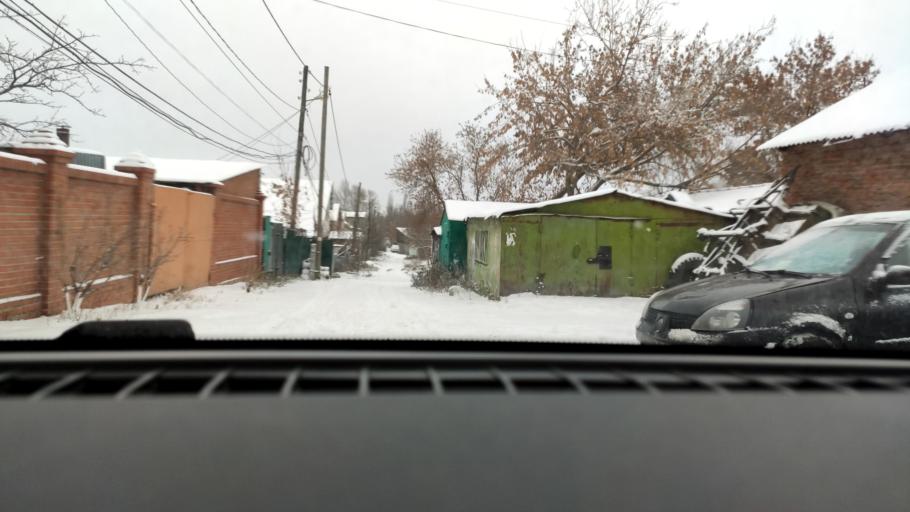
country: RU
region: Samara
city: Samara
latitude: 53.1829
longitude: 50.1550
